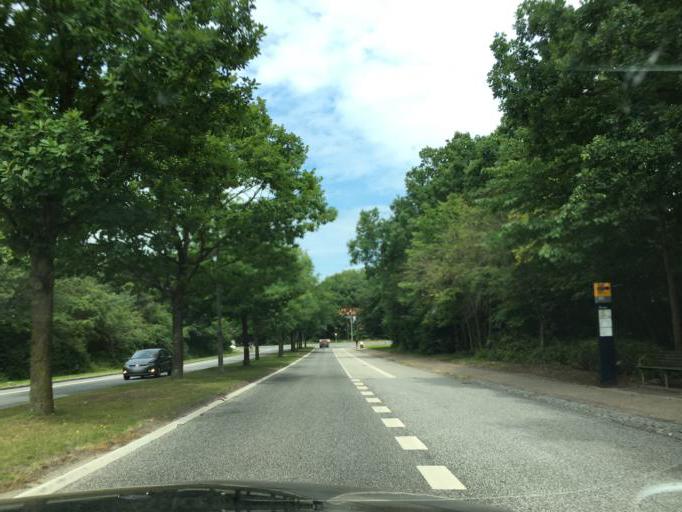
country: DK
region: Capital Region
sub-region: Fredensborg Kommune
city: Kokkedal
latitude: 55.9007
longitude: 12.4976
